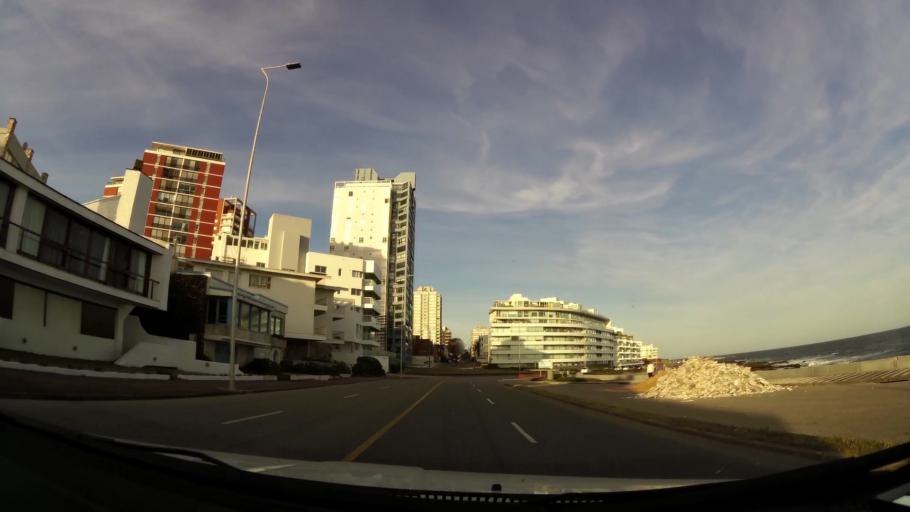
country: UY
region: Maldonado
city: Punta del Este
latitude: -34.9678
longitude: -54.9481
